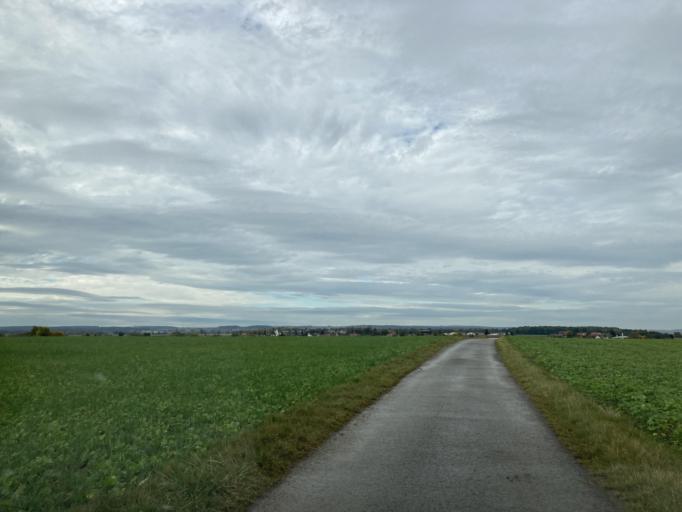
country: DE
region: Baden-Wuerttemberg
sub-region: Regierungsbezirk Stuttgart
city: Bondorf
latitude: 48.5222
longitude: 8.8785
